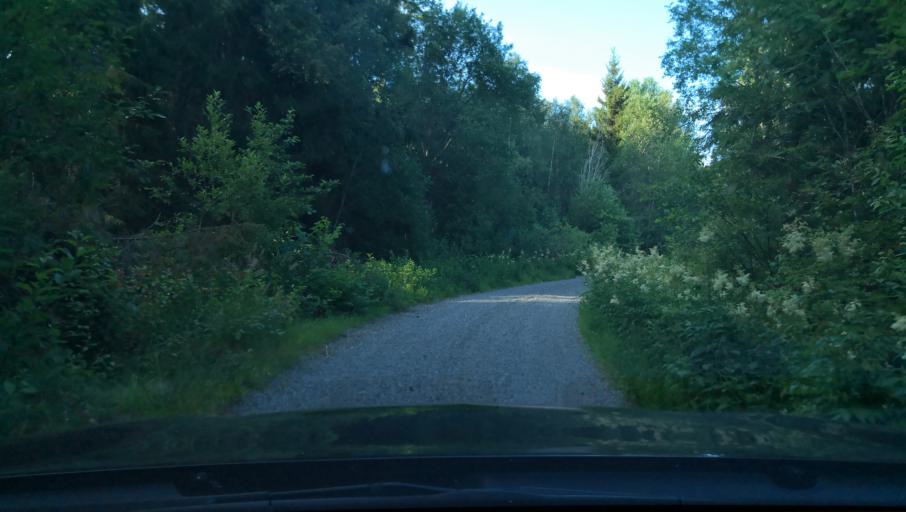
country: SE
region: Uppsala
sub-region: Osthammars Kommun
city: Osterbybruk
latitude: 60.0220
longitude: 17.9172
